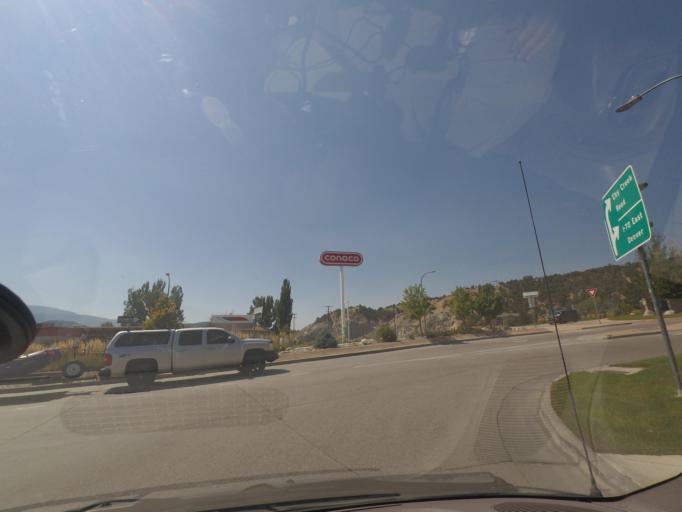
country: US
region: Colorado
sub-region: Eagle County
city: Eagle
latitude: 39.6594
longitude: -106.8266
